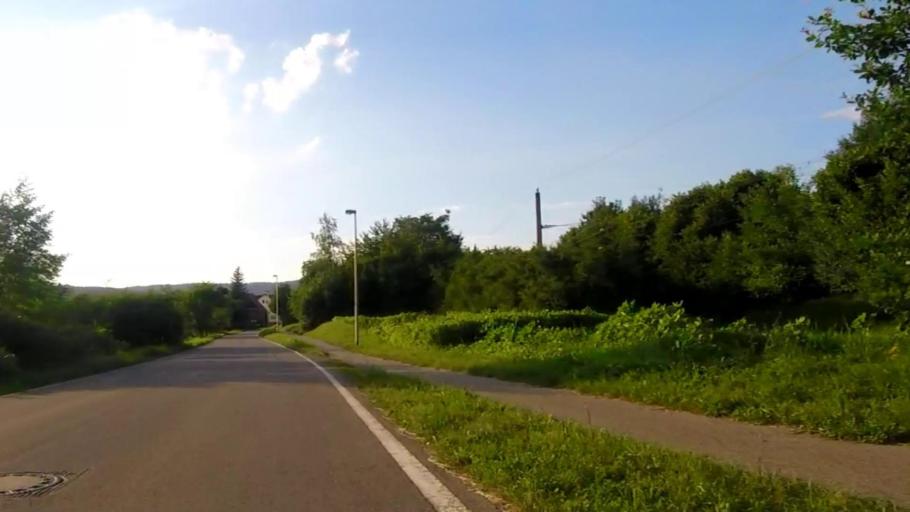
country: DE
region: Baden-Wuerttemberg
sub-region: Regierungsbezirk Stuttgart
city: Oppenweiler
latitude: 48.9751
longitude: 9.4607
